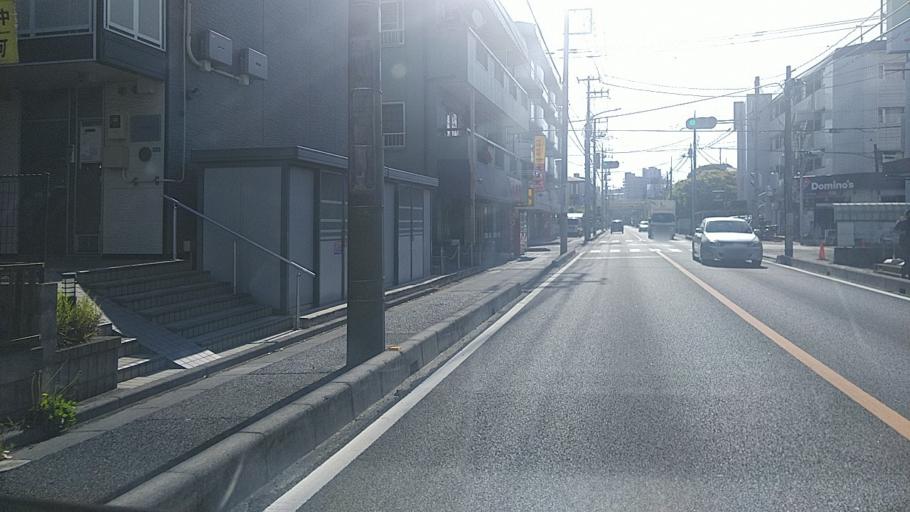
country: JP
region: Saitama
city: Kawaguchi
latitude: 35.8054
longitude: 139.7063
